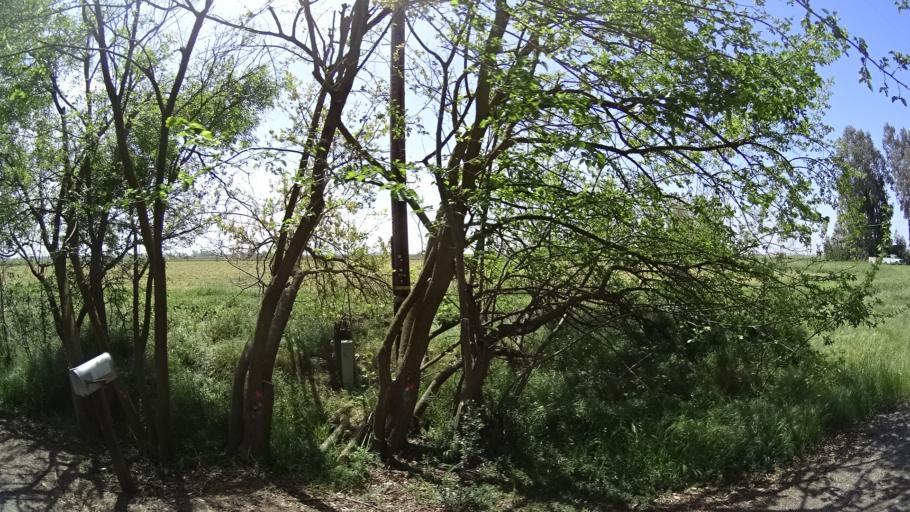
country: US
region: California
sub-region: Glenn County
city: Willows
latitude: 39.5944
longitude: -122.0600
